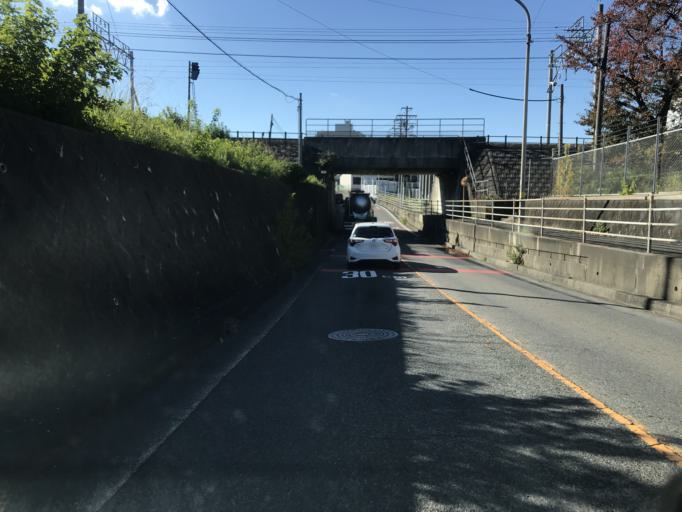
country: JP
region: Aichi
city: Nagoya-shi
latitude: 35.1966
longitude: 136.8511
